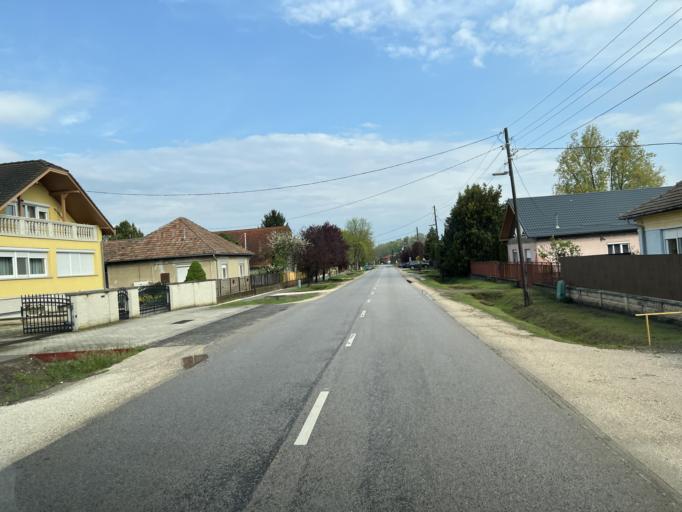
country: HU
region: Pest
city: Nyaregyhaza
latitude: 47.2322
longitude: 19.4483
